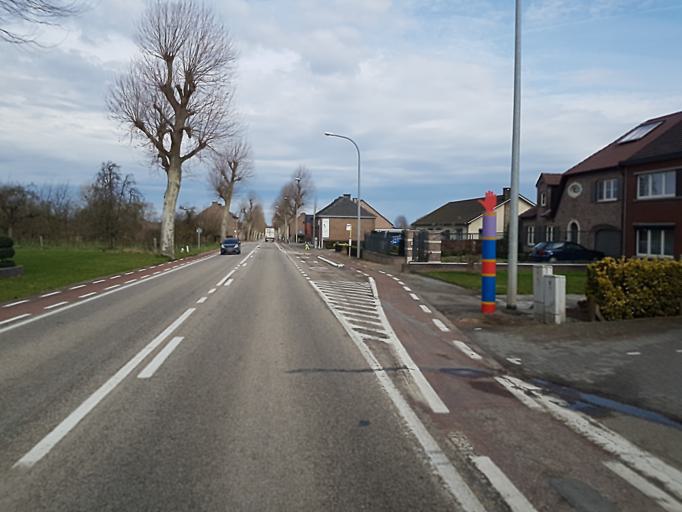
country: BE
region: Flanders
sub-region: Provincie Limburg
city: Kortessem
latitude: 50.8186
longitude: 5.4172
